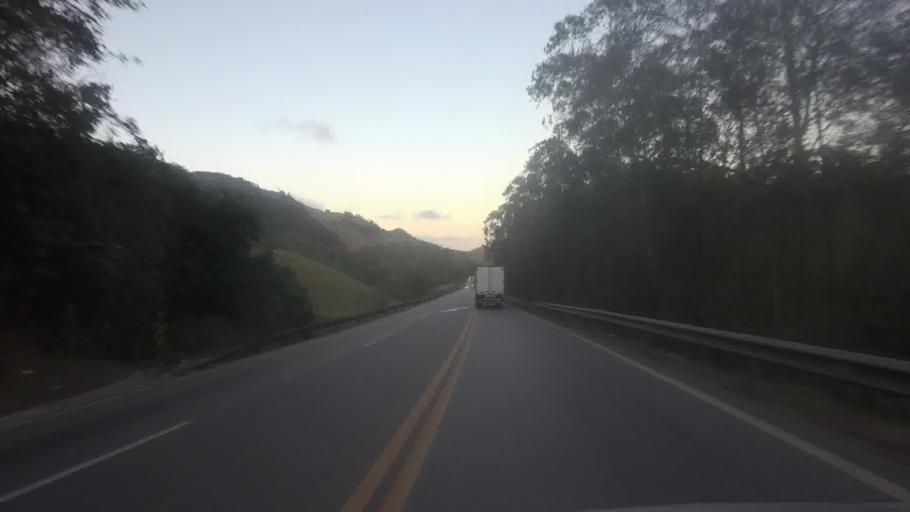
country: BR
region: Espirito Santo
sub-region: Rio Novo Do Sul
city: Rio Novo do Sul
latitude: -20.8660
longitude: -40.9256
